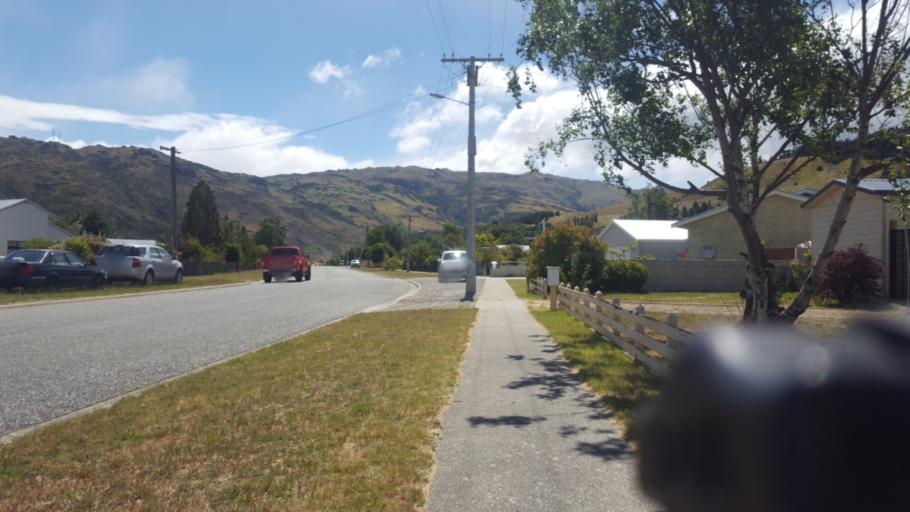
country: NZ
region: Otago
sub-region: Queenstown-Lakes District
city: Wanaka
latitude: -45.1901
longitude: 169.3247
